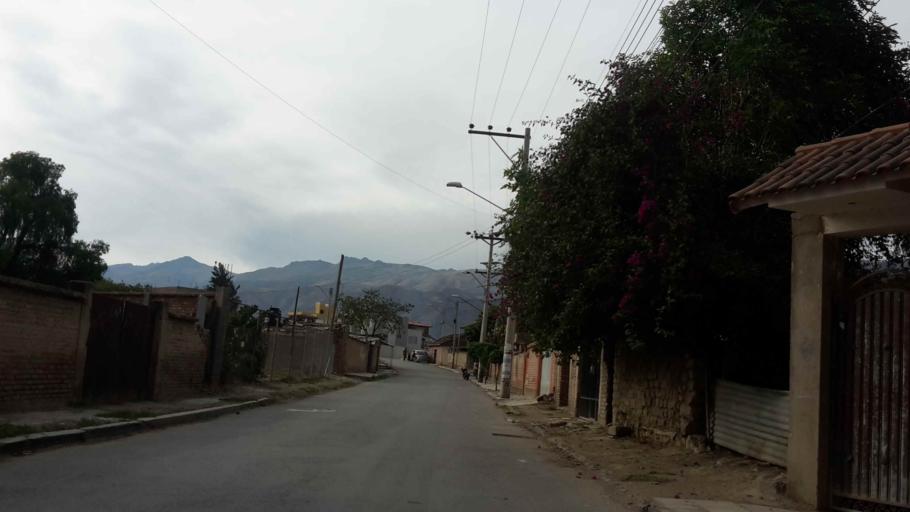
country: BO
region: Cochabamba
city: Cochabamba
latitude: -17.3614
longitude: -66.1905
